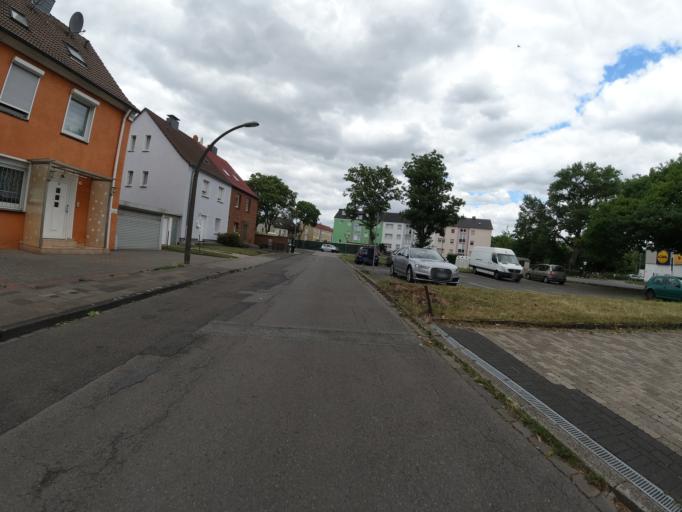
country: DE
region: North Rhine-Westphalia
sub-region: Regierungsbezirk Dusseldorf
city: Hochfeld
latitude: 51.4034
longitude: 6.7233
